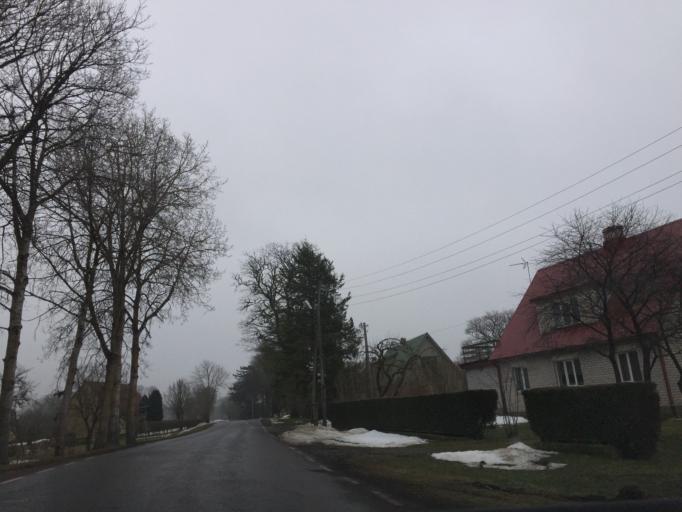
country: EE
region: Saare
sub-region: Orissaare vald
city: Orissaare
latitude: 58.4099
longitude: 22.7944
